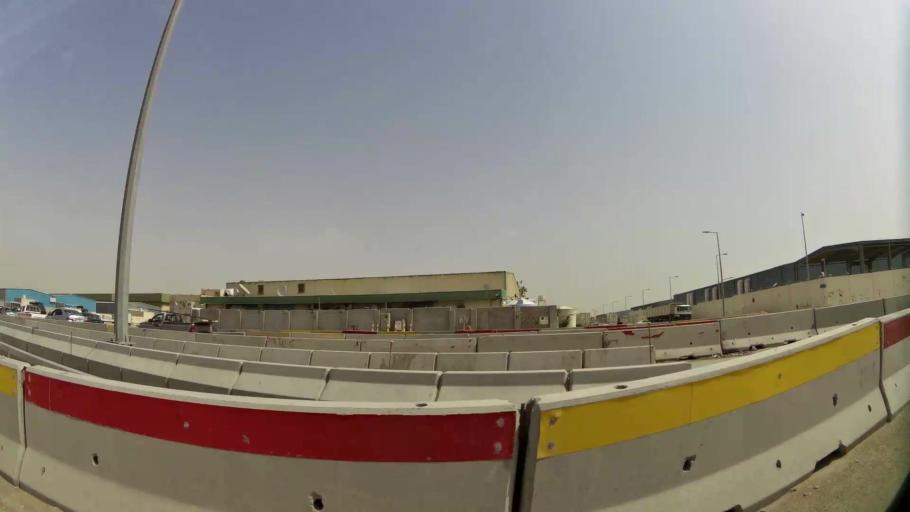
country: QA
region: Baladiyat ar Rayyan
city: Ar Rayyan
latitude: 25.2039
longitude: 51.4111
